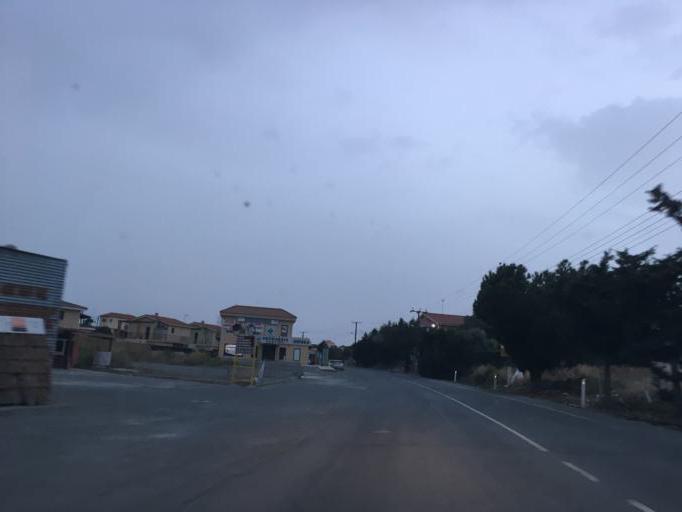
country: CY
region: Limassol
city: Parekklisha
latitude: 34.7455
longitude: 33.1559
